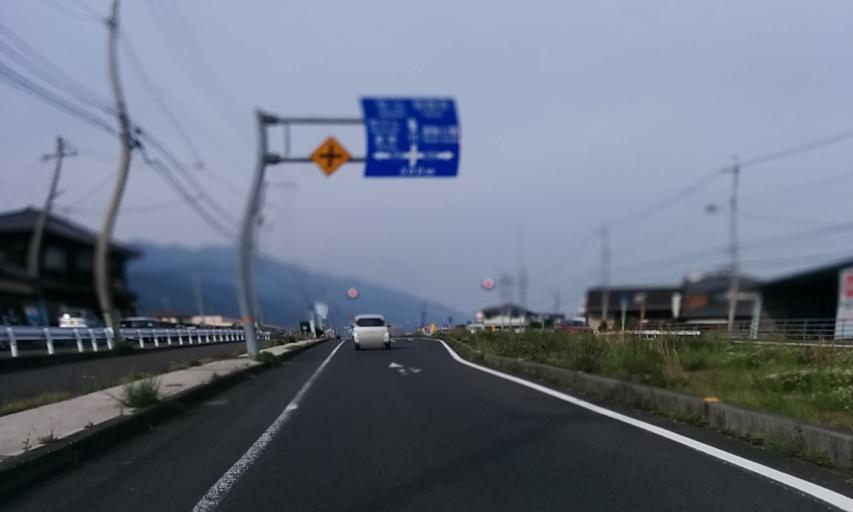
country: JP
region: Ehime
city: Kawanoecho
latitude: 33.9765
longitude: 133.5465
